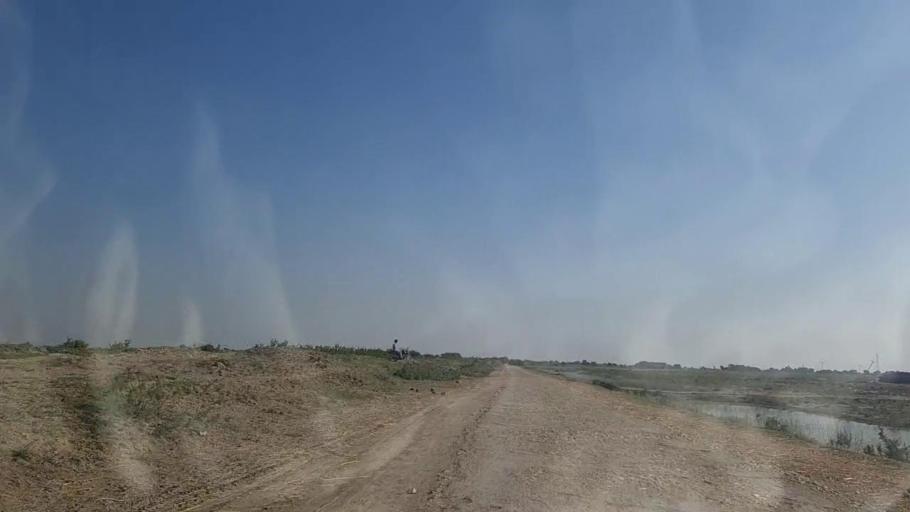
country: PK
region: Sindh
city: Mirpur Batoro
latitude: 24.6096
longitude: 68.1697
